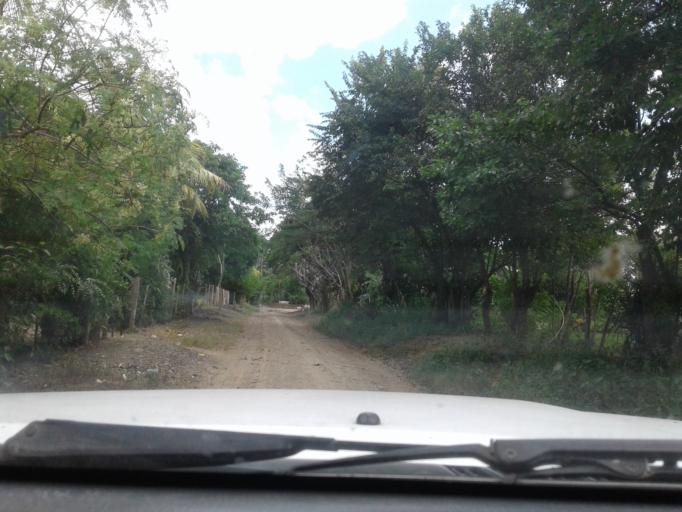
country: NI
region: Rivas
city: Belen
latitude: 11.6277
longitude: -85.9530
